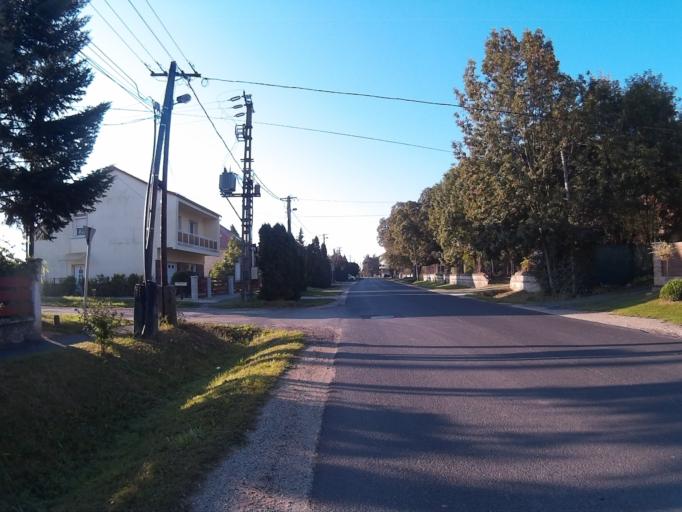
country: HU
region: Vas
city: Jak
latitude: 47.1361
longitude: 16.5839
